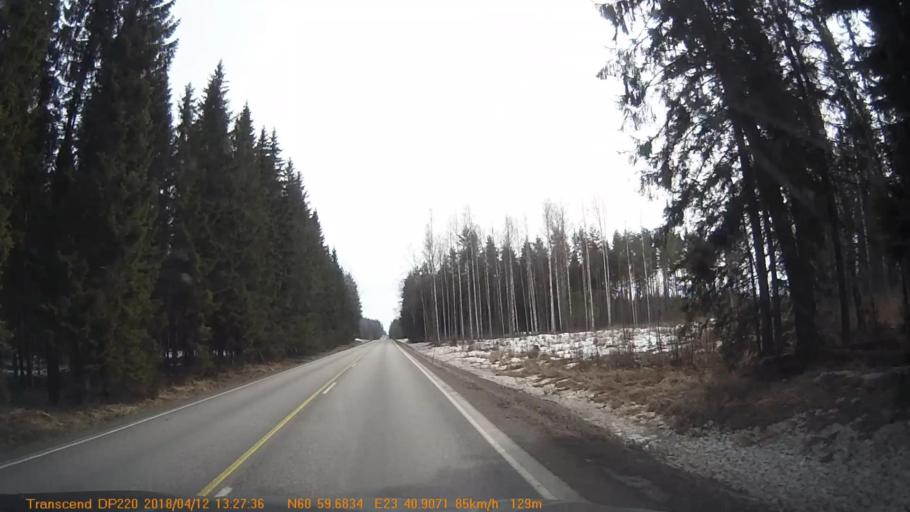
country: FI
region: Pirkanmaa
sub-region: Etelae-Pirkanmaa
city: Kylmaekoski
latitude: 60.9945
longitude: 23.6820
